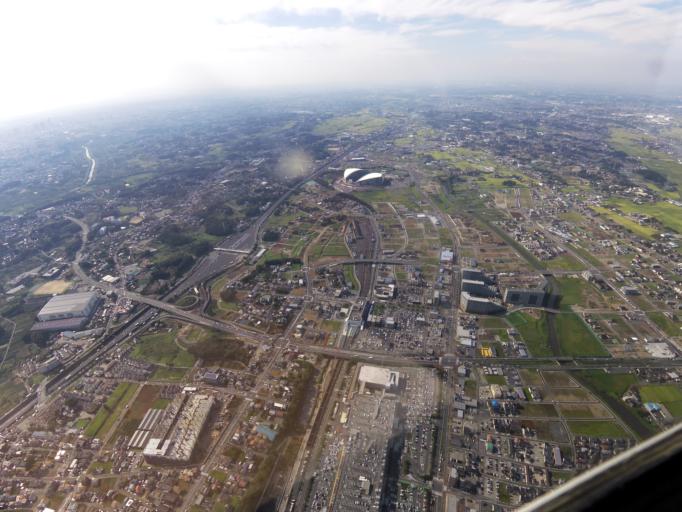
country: JP
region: Saitama
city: Koshigaya
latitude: 35.8886
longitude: 139.7337
